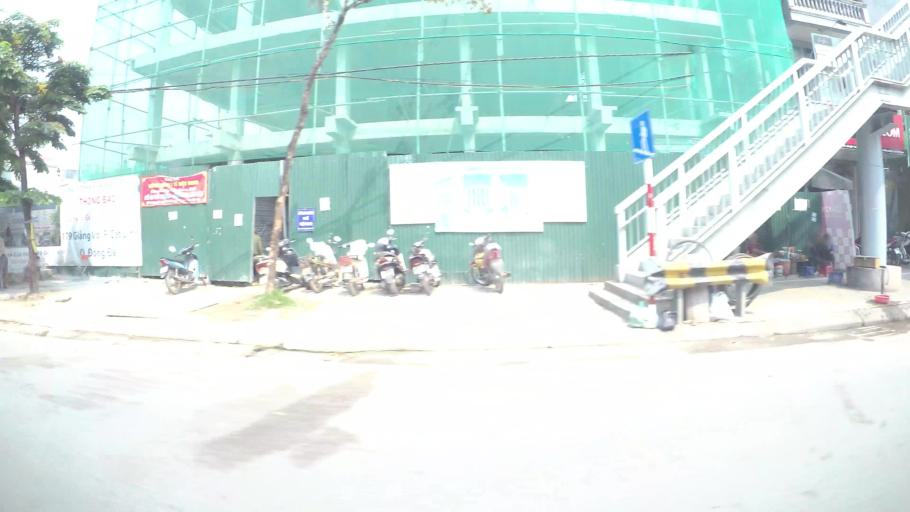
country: VN
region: Ha Noi
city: Dong Da
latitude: 21.0293
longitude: 105.8265
